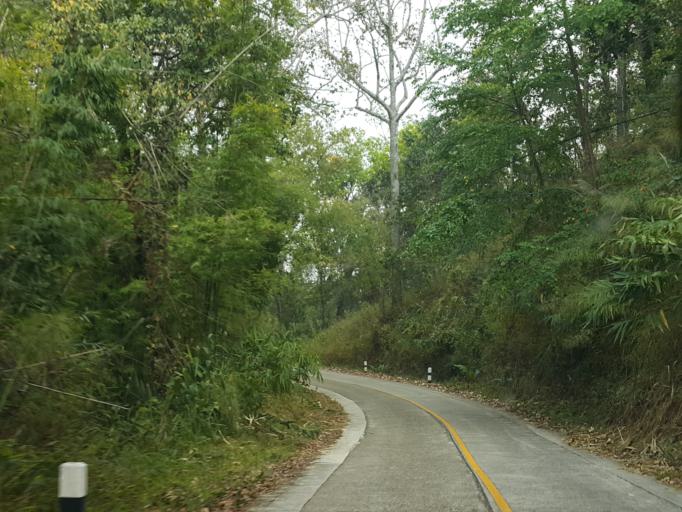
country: TH
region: Chiang Mai
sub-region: Amphoe Chiang Dao
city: Chiang Dao
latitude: 19.4130
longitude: 98.8914
